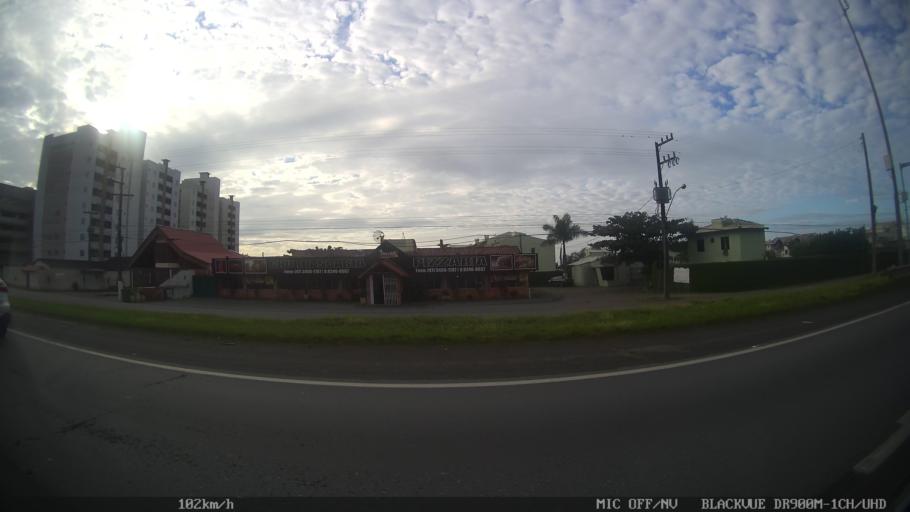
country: BR
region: Santa Catarina
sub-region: Barra Velha
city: Barra Velha
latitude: -26.6688
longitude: -48.6895
